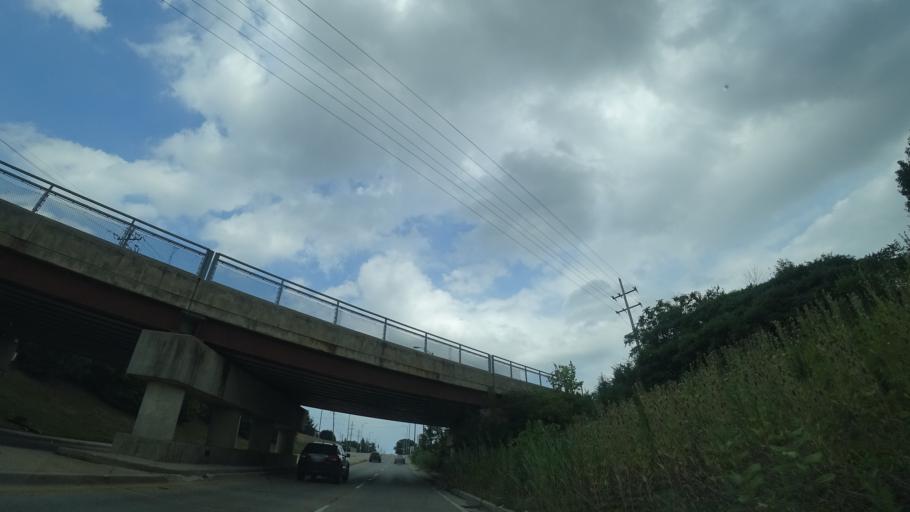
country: US
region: Illinois
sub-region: Cook County
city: Oak Lawn
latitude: 41.6906
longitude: -87.7531
